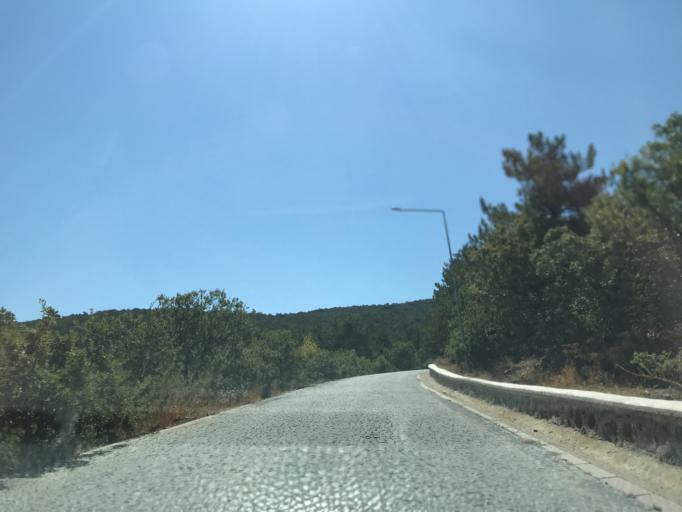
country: TR
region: Yozgat
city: Yozgat
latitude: 39.8090
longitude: 34.8082
